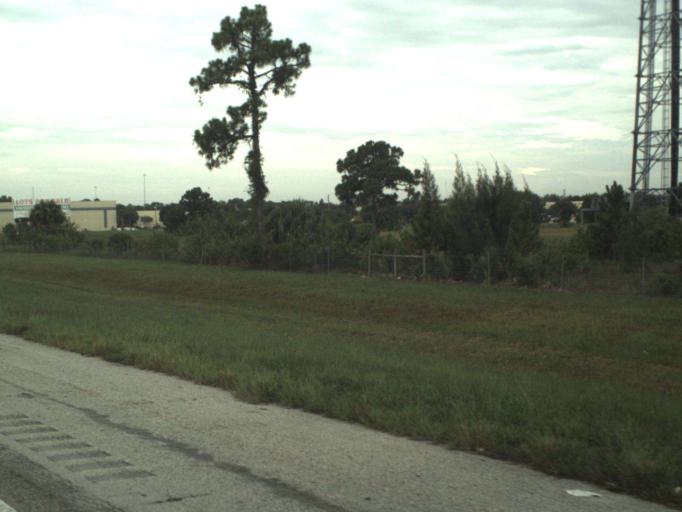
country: US
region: Florida
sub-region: Martin County
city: Palm City
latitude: 27.1145
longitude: -80.2646
